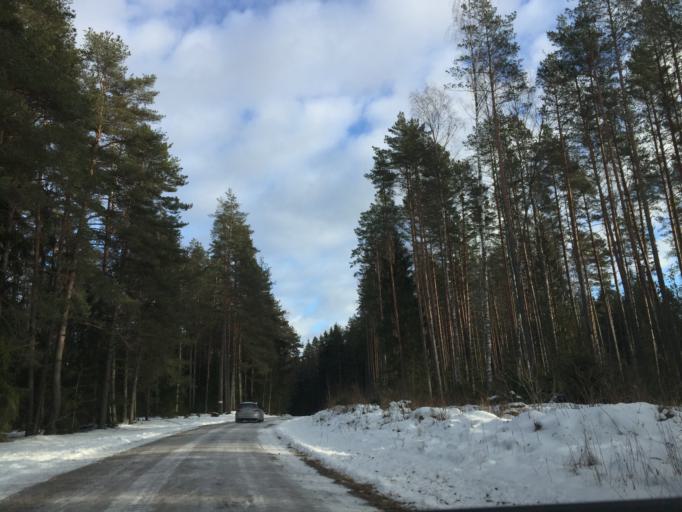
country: LV
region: Lielvarde
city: Lielvarde
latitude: 56.5654
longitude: 24.8116
